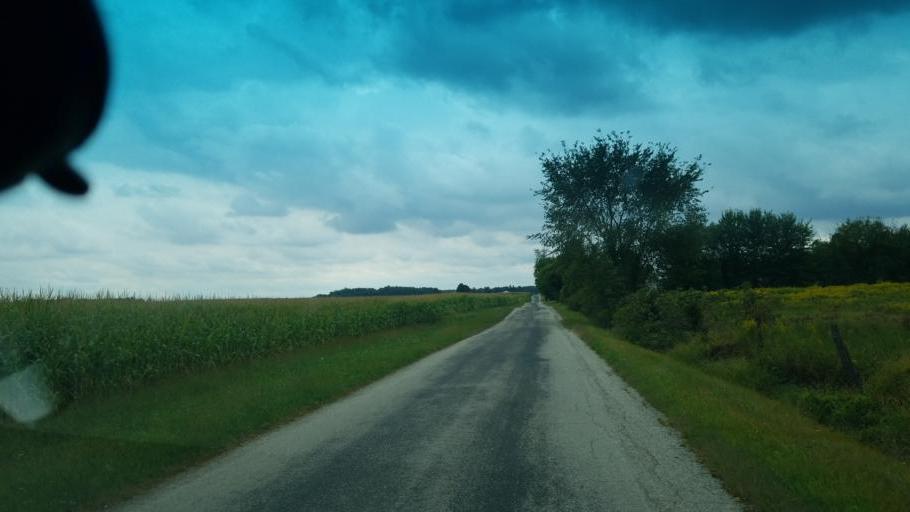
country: US
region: Ohio
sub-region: Richland County
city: Shelby
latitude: 40.8928
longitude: -82.5714
